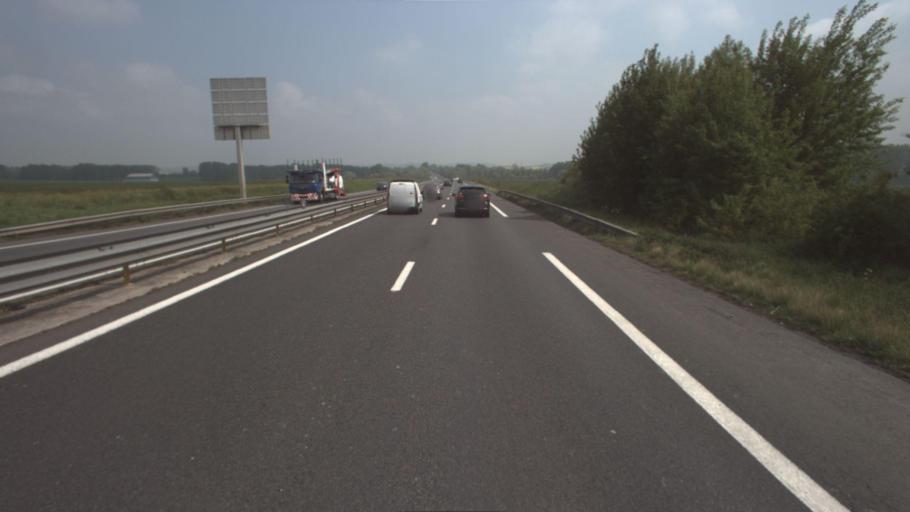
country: FR
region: Ile-de-France
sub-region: Departement de Seine-et-Marne
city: Longperrier
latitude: 49.0097
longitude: 2.6511
